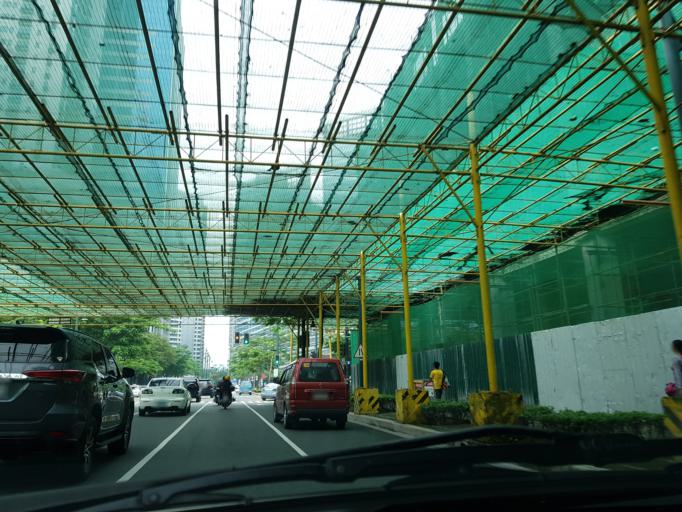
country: PH
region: Metro Manila
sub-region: Makati City
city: Makati City
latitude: 14.5482
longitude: 121.0491
